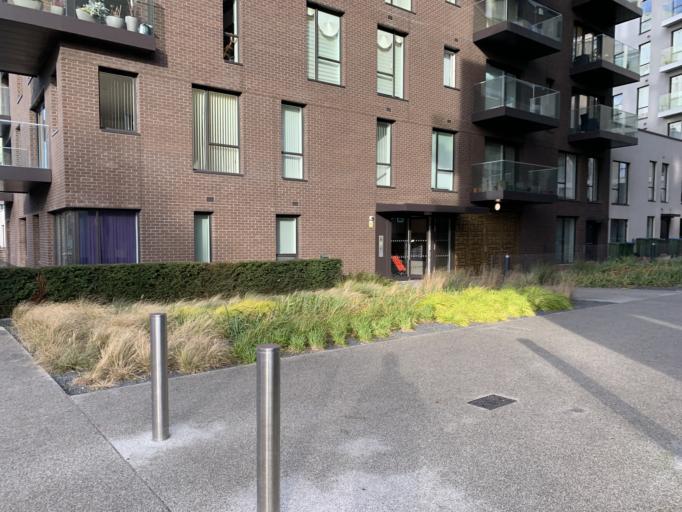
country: GB
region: England
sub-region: Greater London
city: Poplar
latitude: 51.4963
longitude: 0.0112
